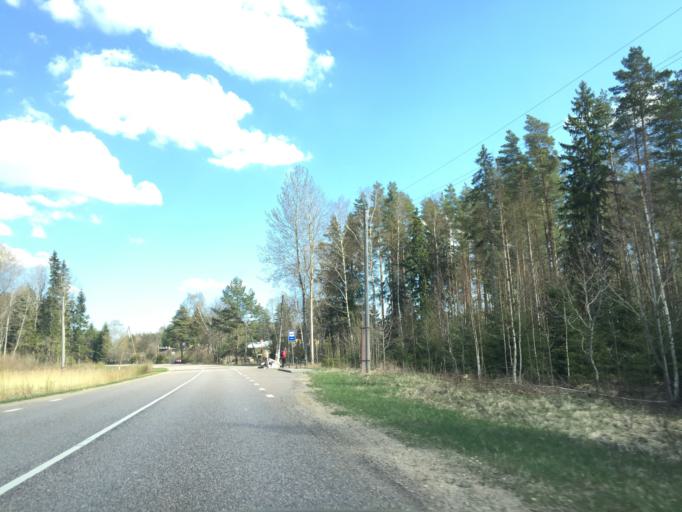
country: LV
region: Saulkrastu
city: Saulkrasti
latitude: 57.2371
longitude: 24.4587
